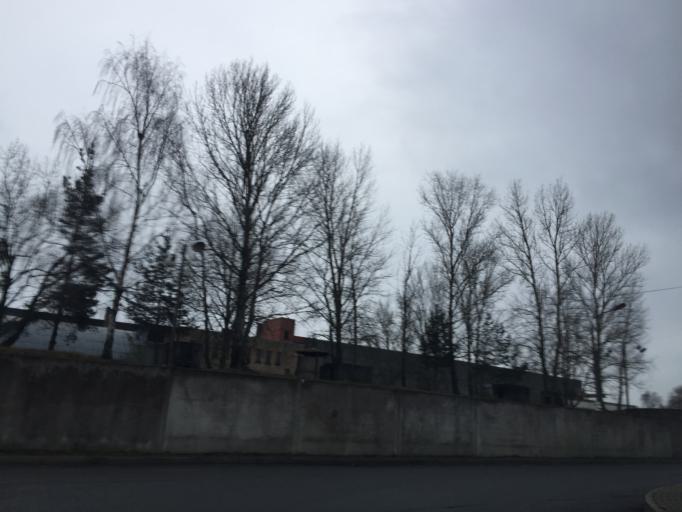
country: LV
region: Riga
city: Riga
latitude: 56.9924
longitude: 24.1158
